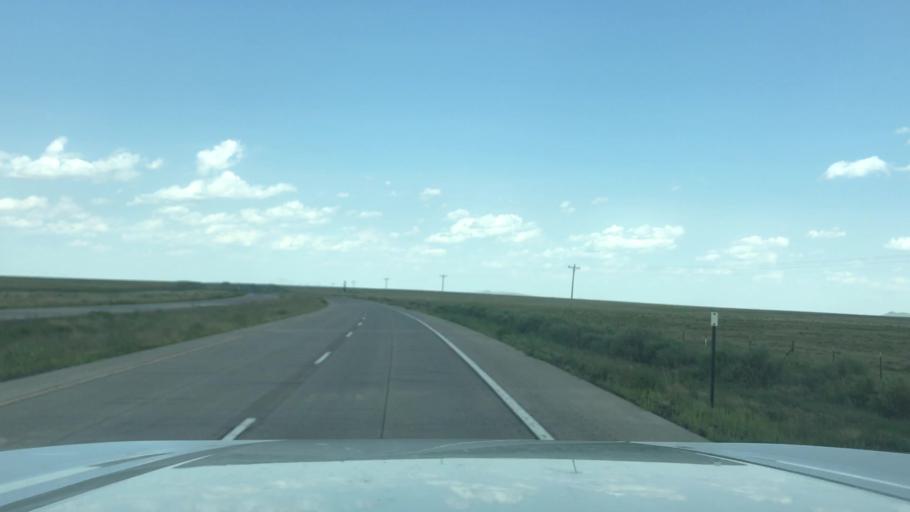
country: US
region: New Mexico
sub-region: Union County
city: Clayton
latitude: 36.6137
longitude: -103.6818
